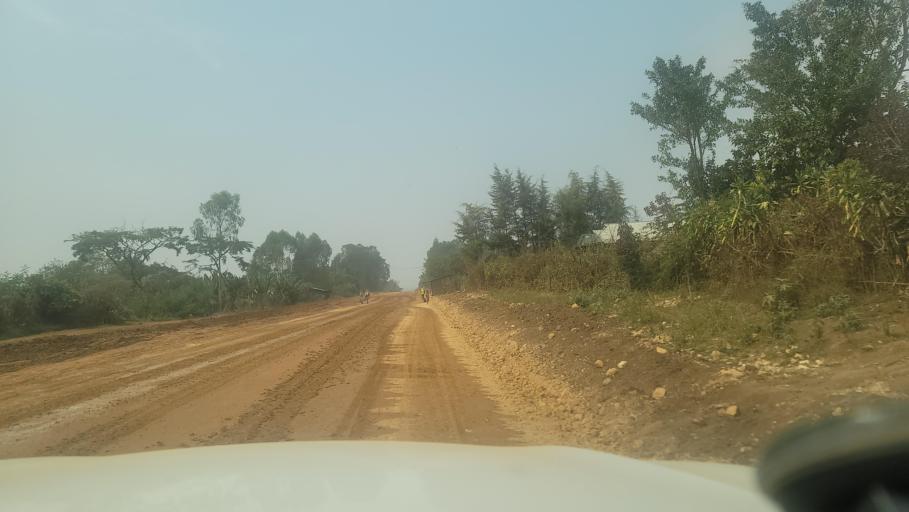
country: ET
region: Oromiya
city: Agaro
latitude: 7.7752
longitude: 36.3265
